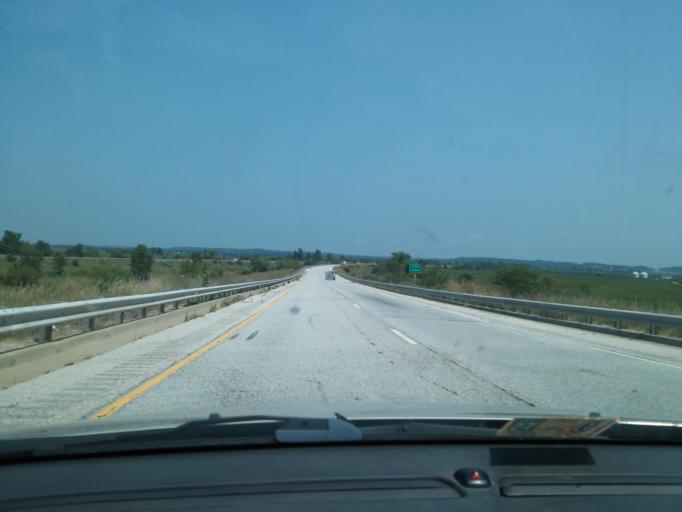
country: US
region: Illinois
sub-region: Pike County
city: Griggsville
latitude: 39.6892
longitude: -90.6342
